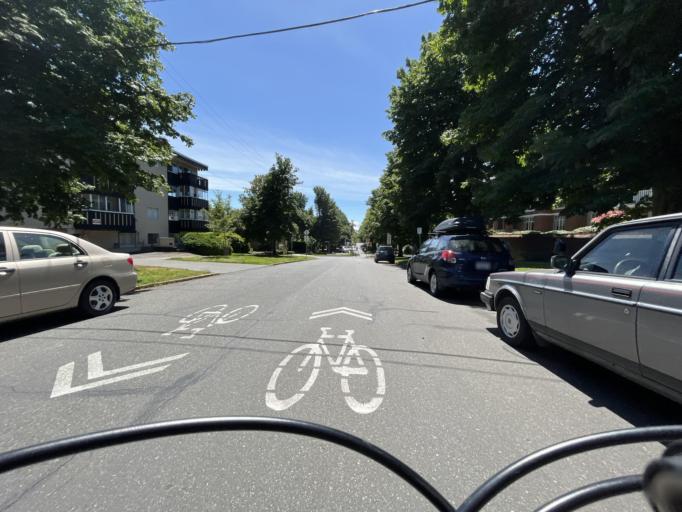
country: CA
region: British Columbia
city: Victoria
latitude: 48.4212
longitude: -123.3576
